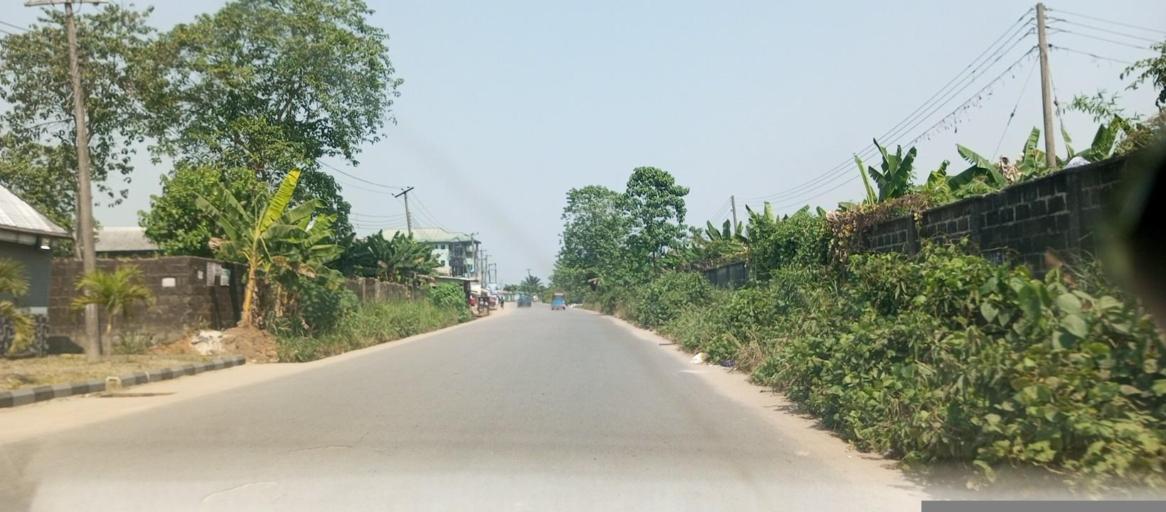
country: NG
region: Rivers
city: Emuoha
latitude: 4.9078
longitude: 6.9092
